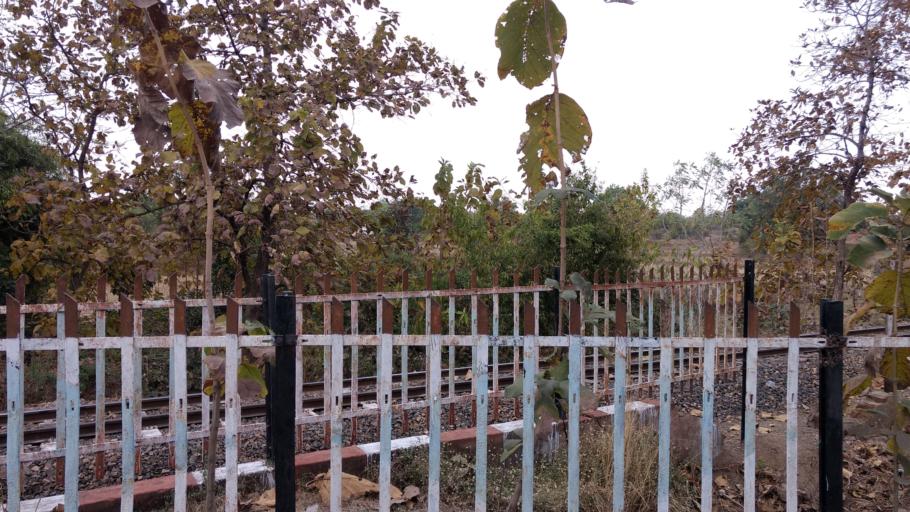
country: IN
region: Maharashtra
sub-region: Nagpur Division
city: Umred
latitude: 20.8017
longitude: 79.4149
